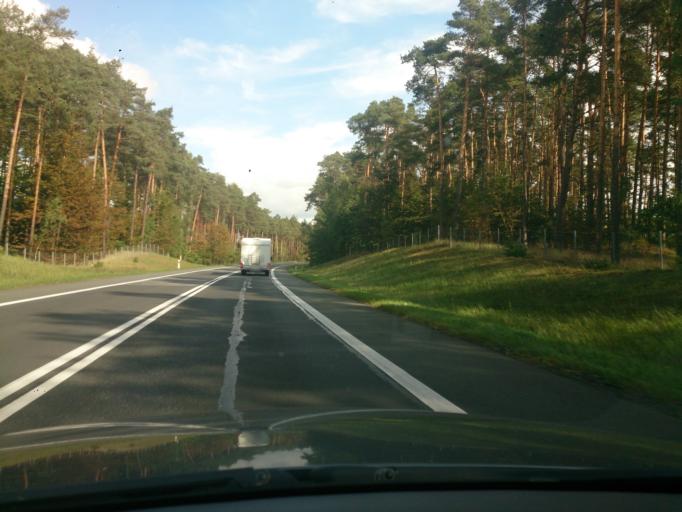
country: PL
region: Kujawsko-Pomorskie
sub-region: Powiat chelminski
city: Chelmno
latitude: 53.3988
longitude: 18.3514
